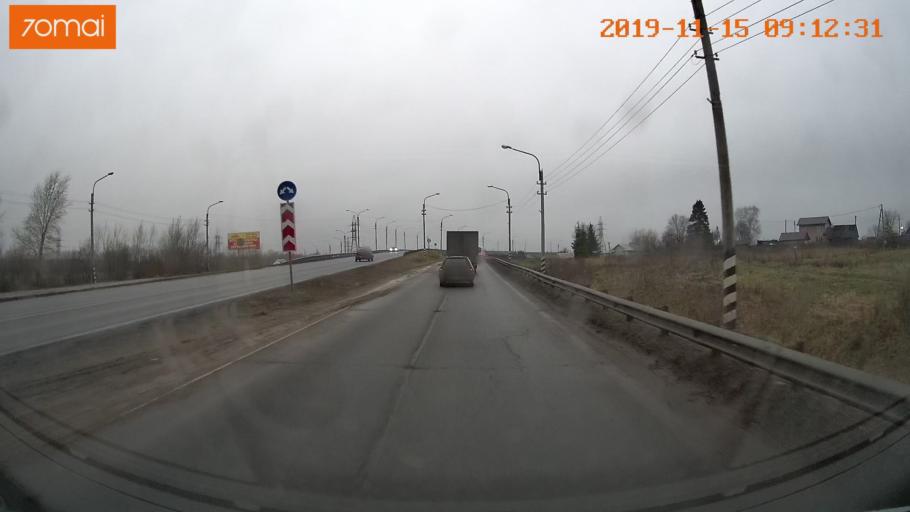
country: RU
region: Vologda
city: Tonshalovo
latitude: 59.2089
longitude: 37.9362
